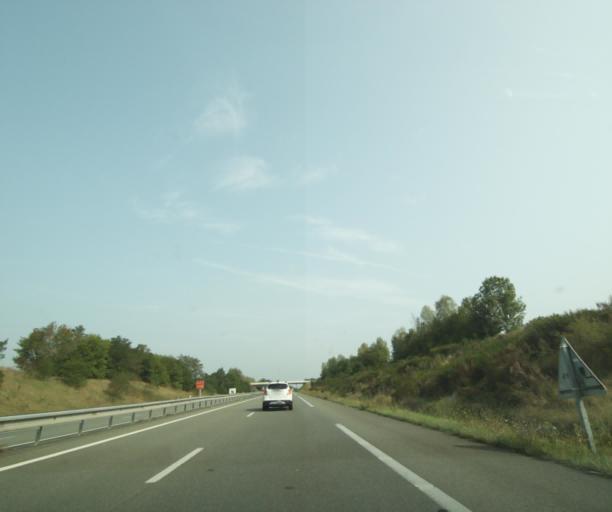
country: FR
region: Pays de la Loire
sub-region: Departement de la Sarthe
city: Neuville-sur-Sarthe
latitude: 48.0668
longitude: 0.1730
